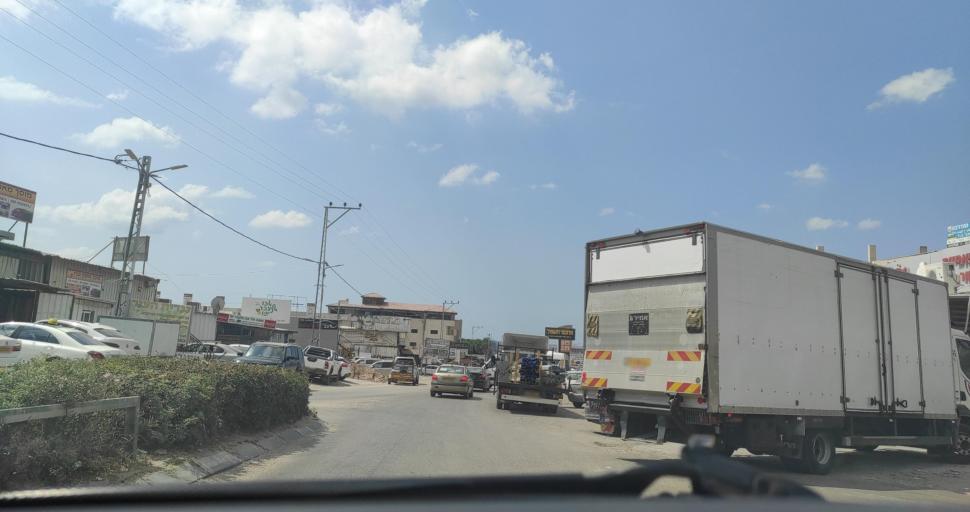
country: IL
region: Central District
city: Kafr Qasim
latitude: 32.1128
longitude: 34.9630
